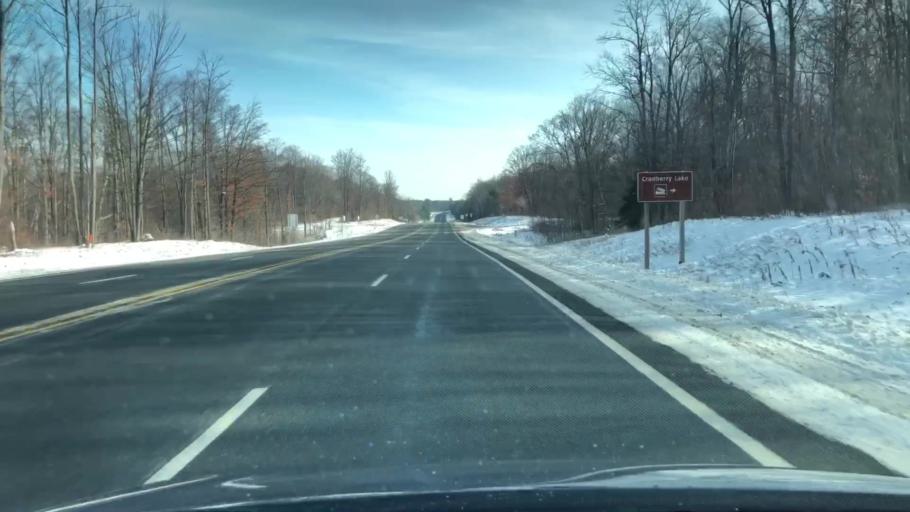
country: US
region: Michigan
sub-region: Kalkaska County
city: Kalkaska
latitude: 44.7129
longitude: -84.9787
